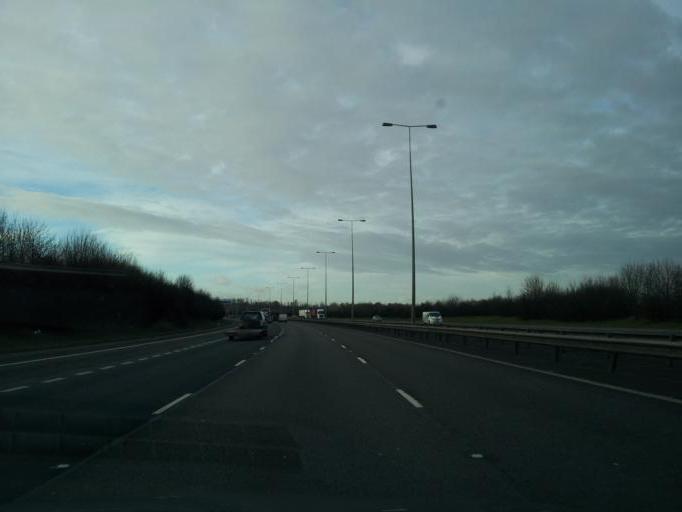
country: GB
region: England
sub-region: Cambridgeshire
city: Stilton
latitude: 52.4907
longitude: -0.2853
